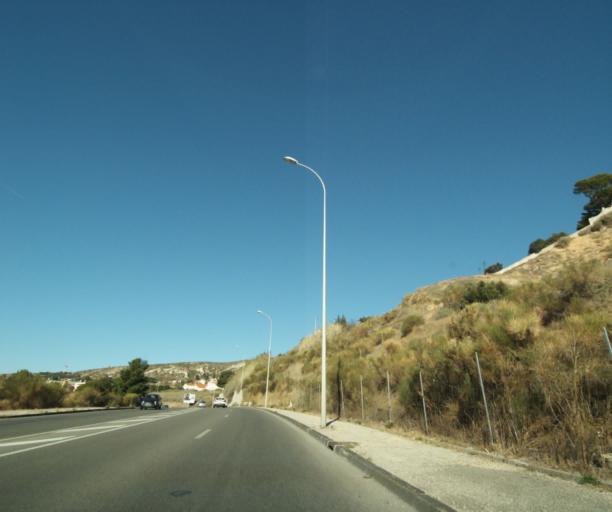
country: FR
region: Provence-Alpes-Cote d'Azur
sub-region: Departement des Bouches-du-Rhone
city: Marseille 16
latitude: 43.3574
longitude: 5.3271
